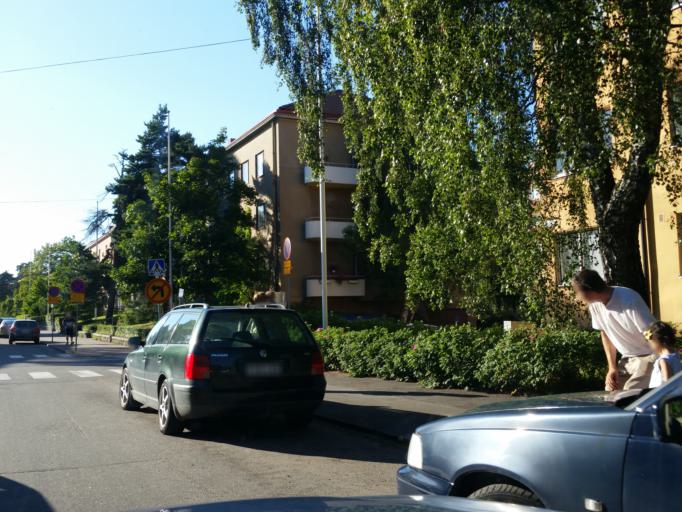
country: FI
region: Uusimaa
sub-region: Helsinki
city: Helsinki
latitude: 60.1928
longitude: 24.9056
